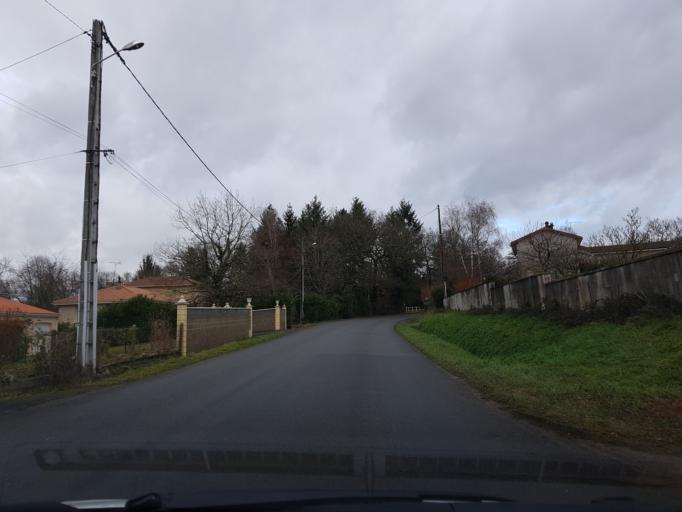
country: FR
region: Poitou-Charentes
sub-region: Departement de la Charente
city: Chabanais
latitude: 45.8834
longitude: 0.7209
